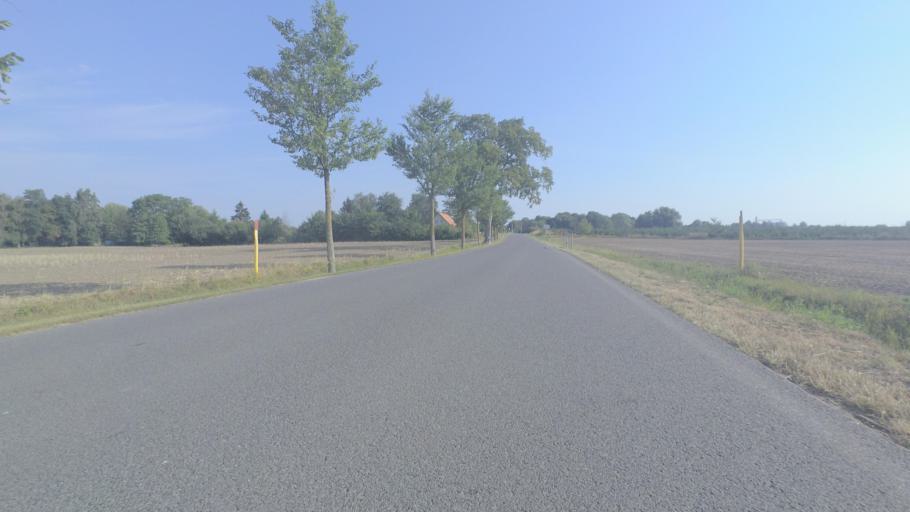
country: DE
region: Mecklenburg-Vorpommern
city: Wittenhagen
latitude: 54.1515
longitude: 13.0717
